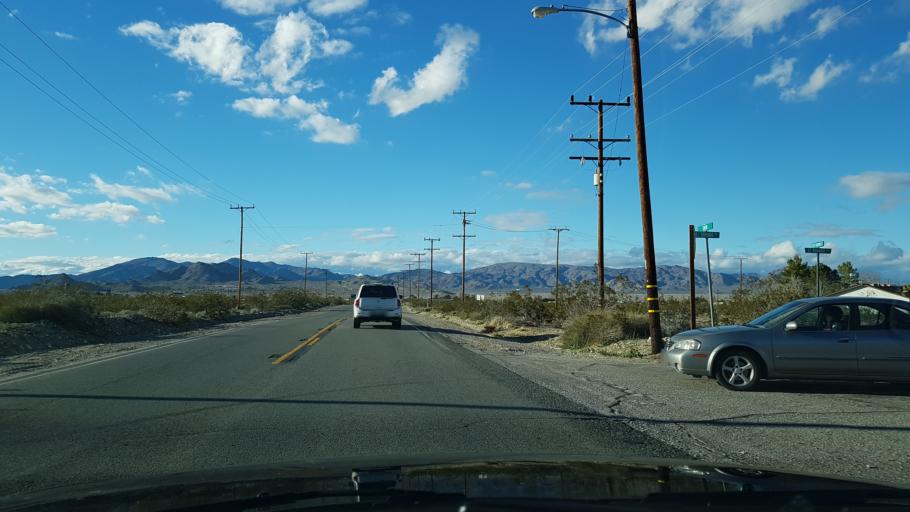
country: US
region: California
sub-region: San Bernardino County
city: Lucerne Valley
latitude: 34.4332
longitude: -116.9363
